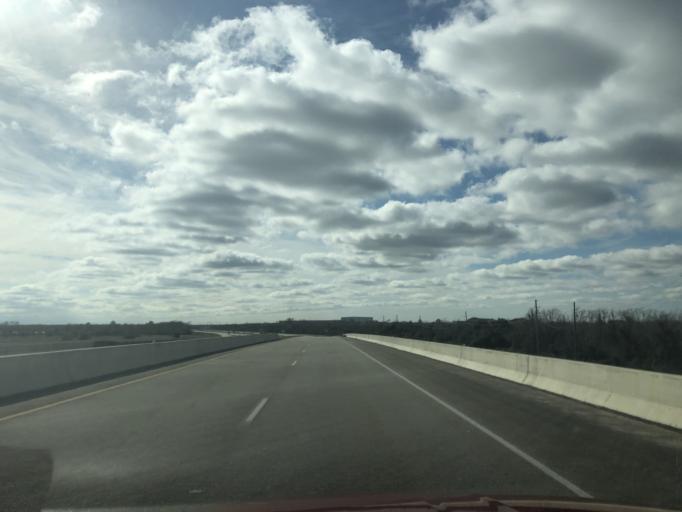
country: US
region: Texas
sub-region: Chambers County
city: Mont Belvieu
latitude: 29.7853
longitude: -94.8721
